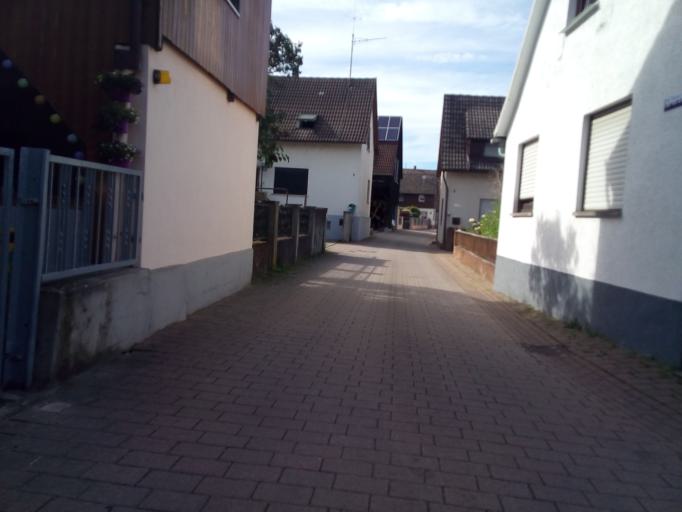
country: DE
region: Baden-Wuerttemberg
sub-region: Karlsruhe Region
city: Lichtenau
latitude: 48.7271
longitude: 8.0049
